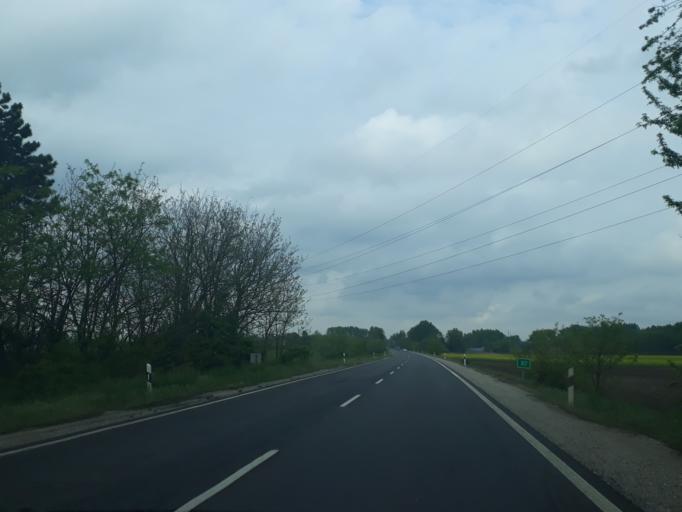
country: HU
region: Szabolcs-Szatmar-Bereg
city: Kisvarda
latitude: 48.2114
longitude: 22.0546
